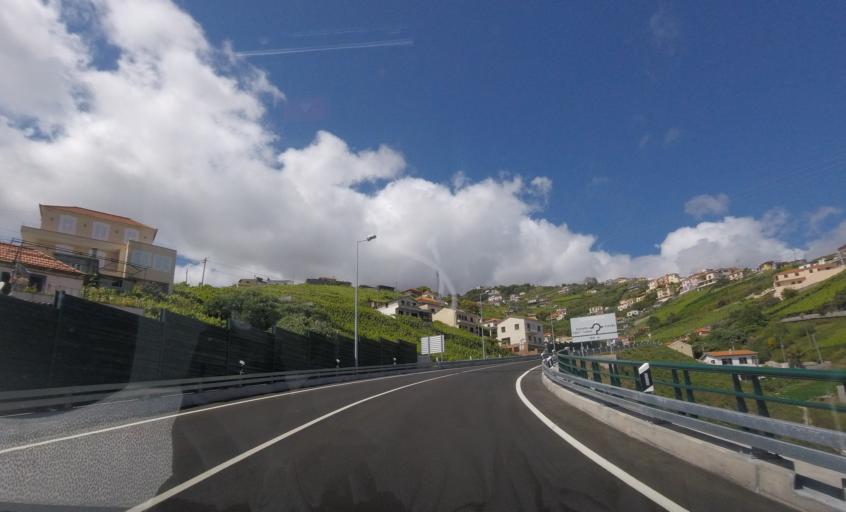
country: PT
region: Madeira
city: Camara de Lobos
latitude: 32.6729
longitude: -16.9745
